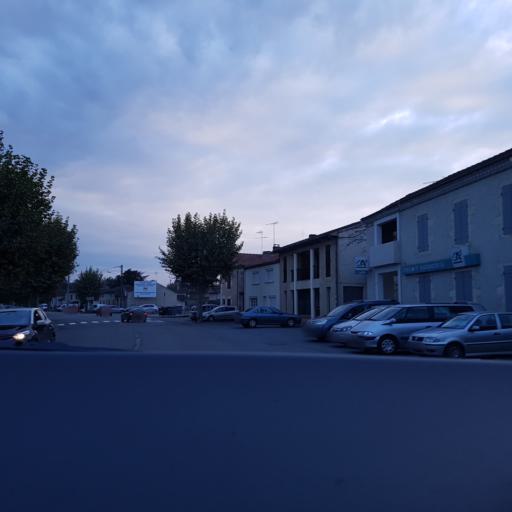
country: FR
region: Midi-Pyrenees
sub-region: Departement du Gers
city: Condom
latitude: 43.9576
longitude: 0.3661
